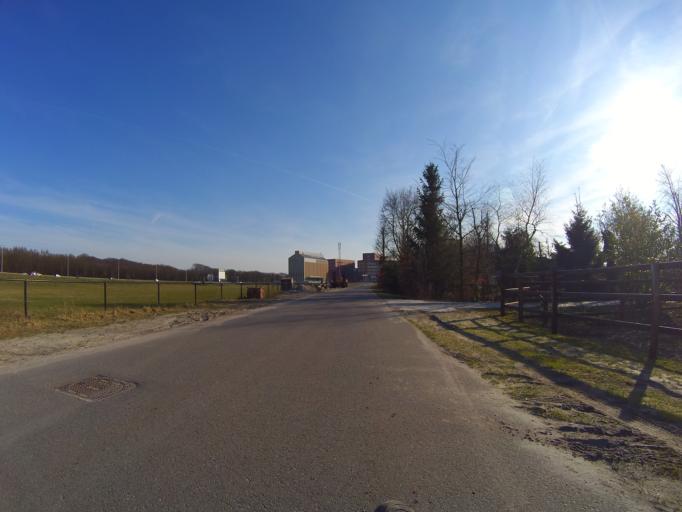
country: NL
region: Gelderland
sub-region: Gemeente Nijkerk
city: Nijkerk
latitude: 52.1933
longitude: 5.4372
